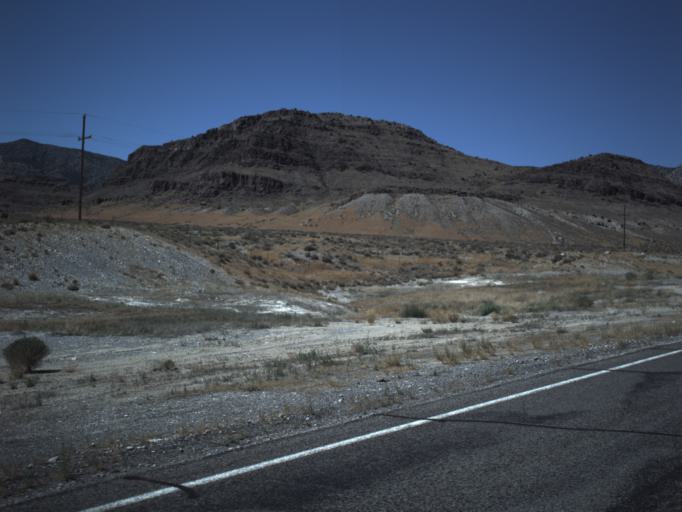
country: US
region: Utah
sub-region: Beaver County
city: Milford
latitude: 39.0845
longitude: -113.5094
